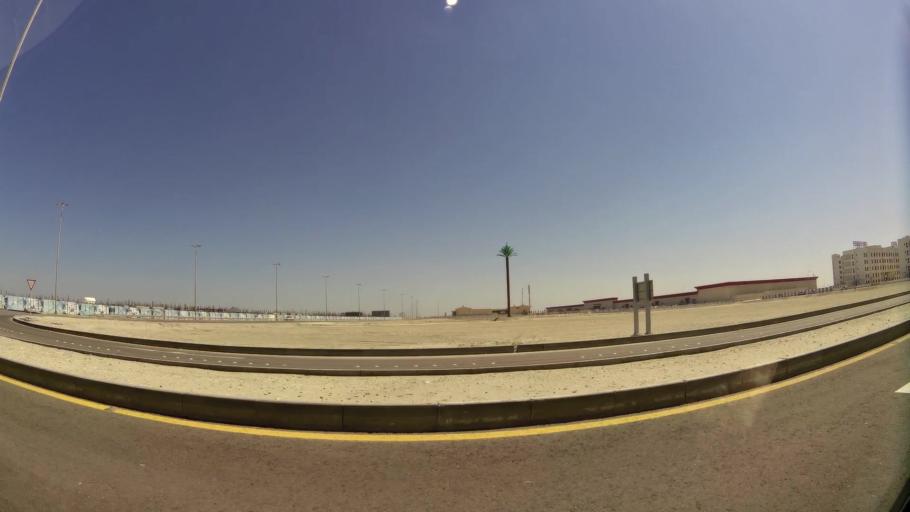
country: BH
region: Muharraq
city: Al Muharraq
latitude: 26.3102
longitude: 50.6223
